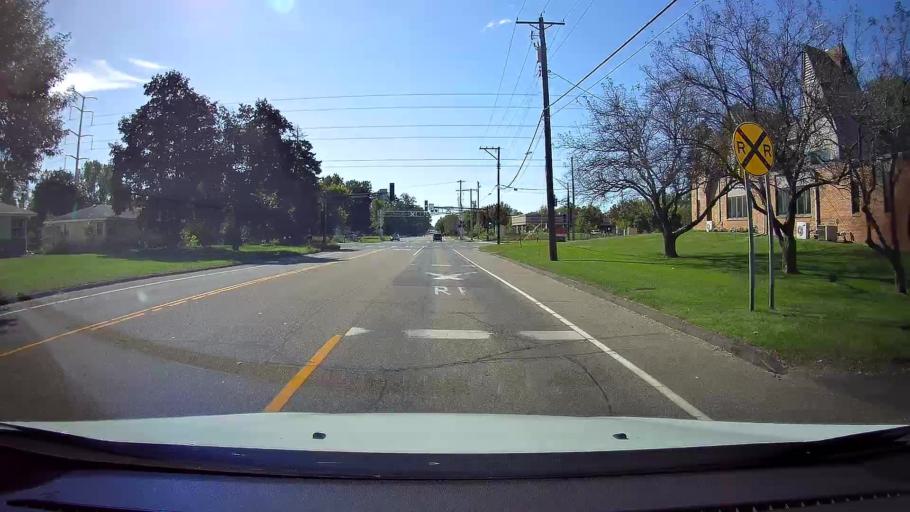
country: US
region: Minnesota
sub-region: Ramsey County
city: Roseville
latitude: 45.0213
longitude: -93.1569
